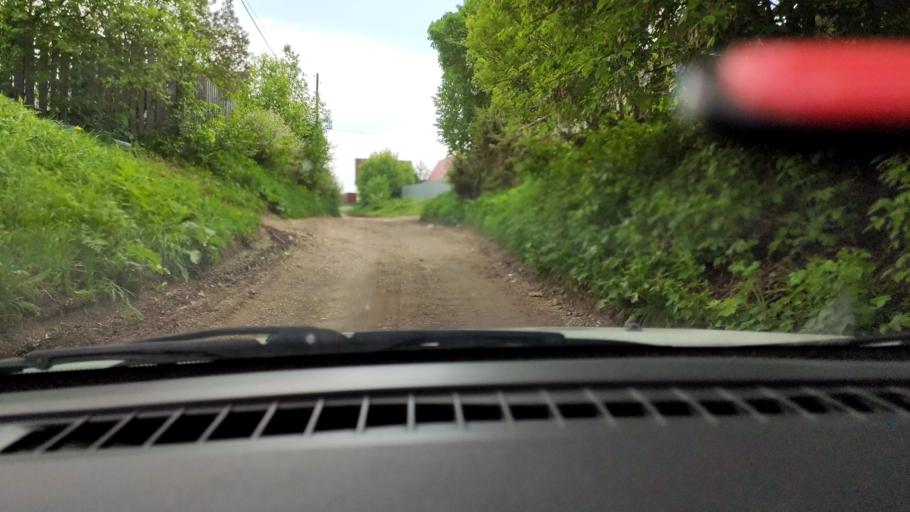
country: RU
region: Perm
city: Bershet'
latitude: 57.7271
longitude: 56.3832
